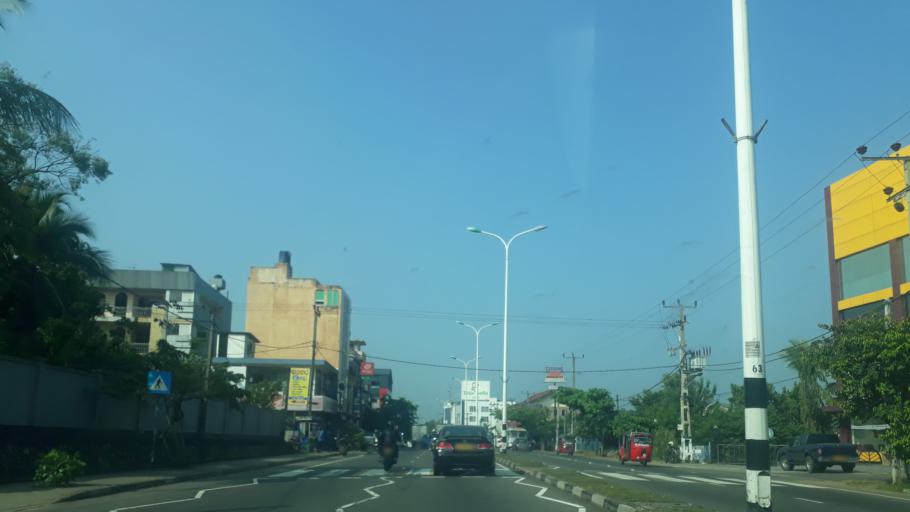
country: LK
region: Western
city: Kelaniya
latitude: 6.9949
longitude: 79.9458
